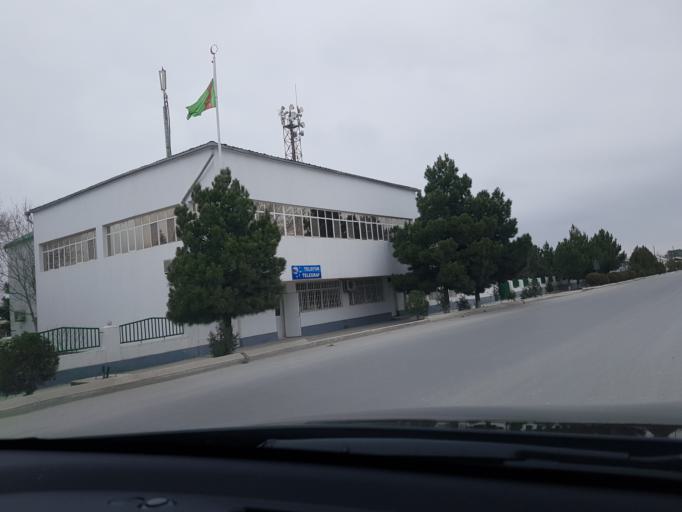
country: TM
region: Ahal
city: Abadan
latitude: 38.1528
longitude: 57.9592
